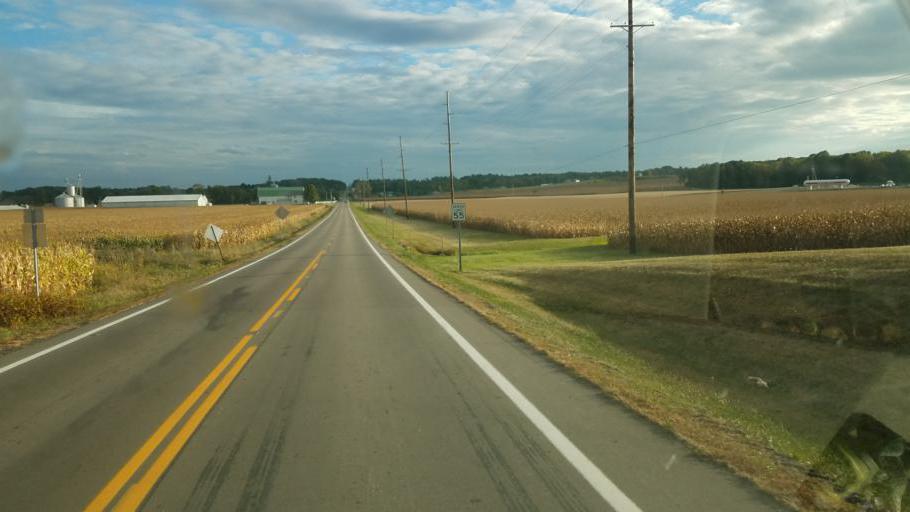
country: US
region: Ohio
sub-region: Ashland County
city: Loudonville
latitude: 40.7840
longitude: -82.1848
